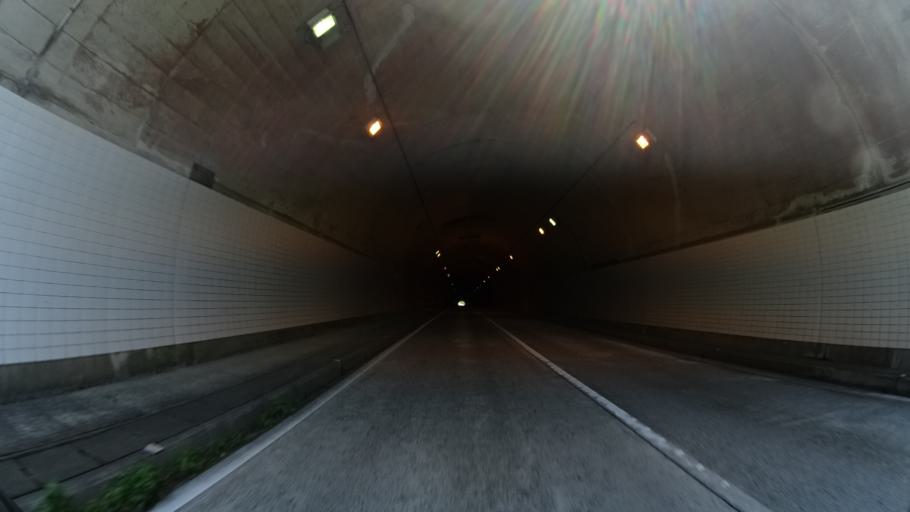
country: JP
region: Ehime
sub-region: Nishiuwa-gun
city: Ikata-cho
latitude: 33.4416
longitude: 132.2455
